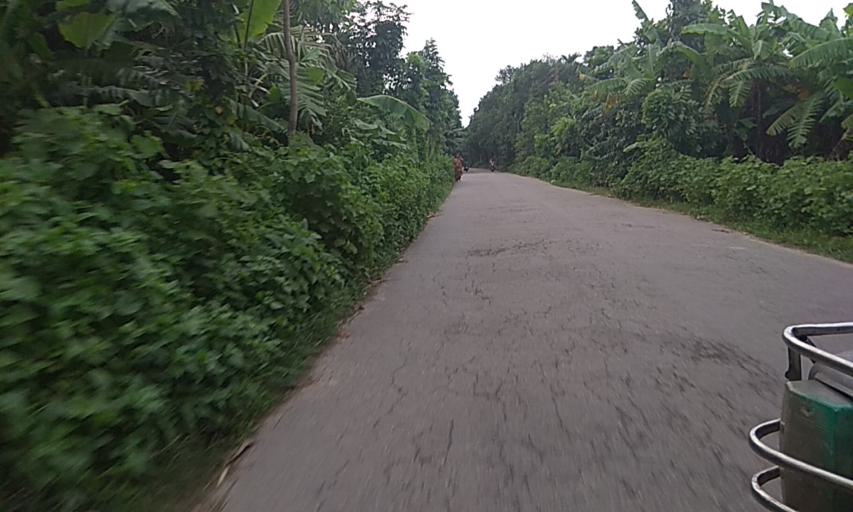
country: BD
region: Dhaka
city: Dohar
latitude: 23.4595
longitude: 89.9988
